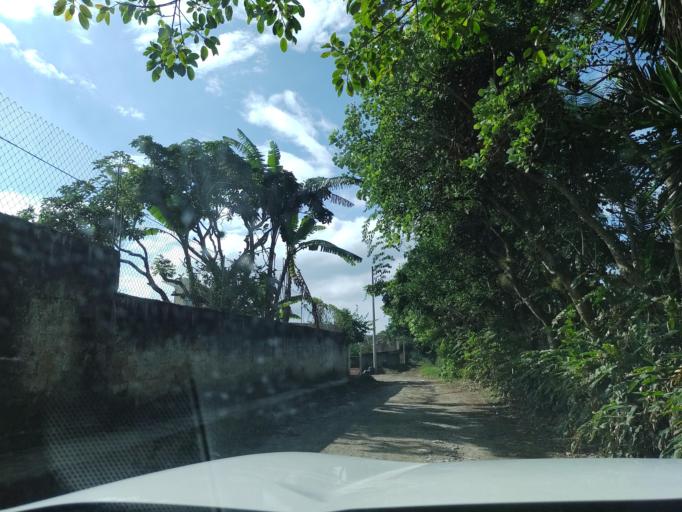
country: MX
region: Veracruz
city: Coatepec
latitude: 19.4813
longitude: -96.9361
